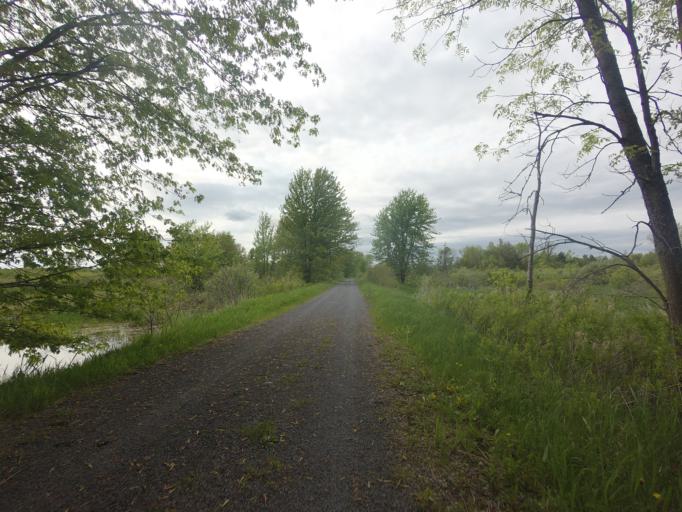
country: CA
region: Ontario
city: Kingston
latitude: 44.3712
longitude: -76.6343
